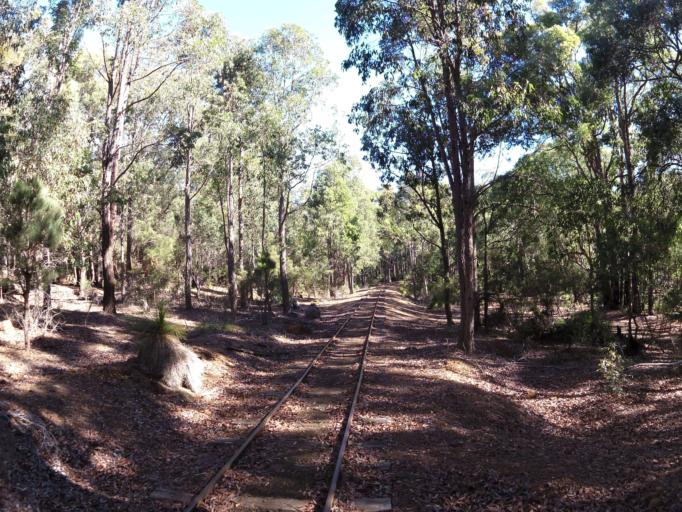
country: AU
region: Western Australia
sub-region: Waroona
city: Waroona
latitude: -32.7110
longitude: 116.0774
